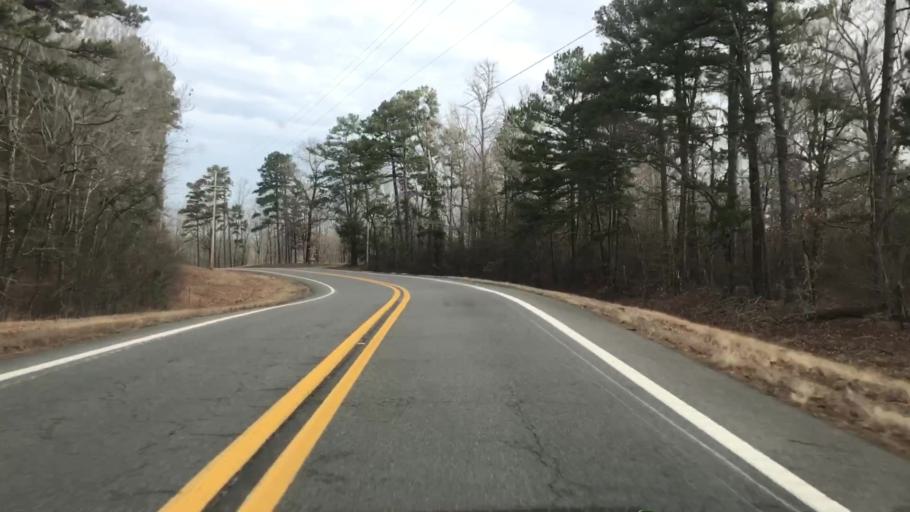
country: US
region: Arkansas
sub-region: Montgomery County
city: Mount Ida
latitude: 34.6146
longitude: -93.7033
